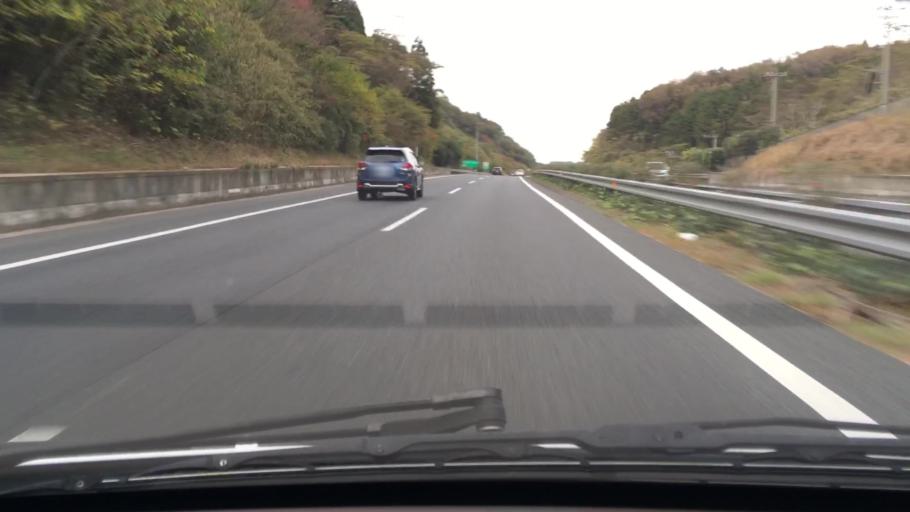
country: JP
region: Chiba
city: Kisarazu
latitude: 35.3325
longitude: 139.9455
